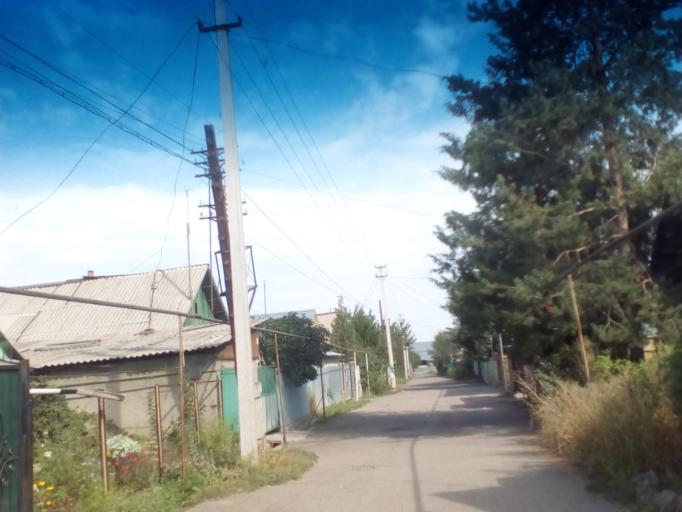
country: KZ
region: Almaty Oblysy
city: Burunday
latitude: 43.1622
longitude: 76.4075
